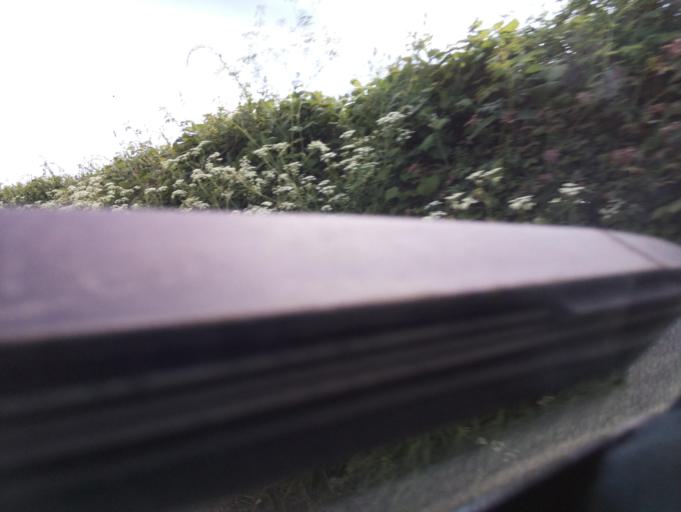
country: GB
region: England
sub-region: Herefordshire
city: Llanrothal
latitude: 51.8373
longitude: -2.7645
